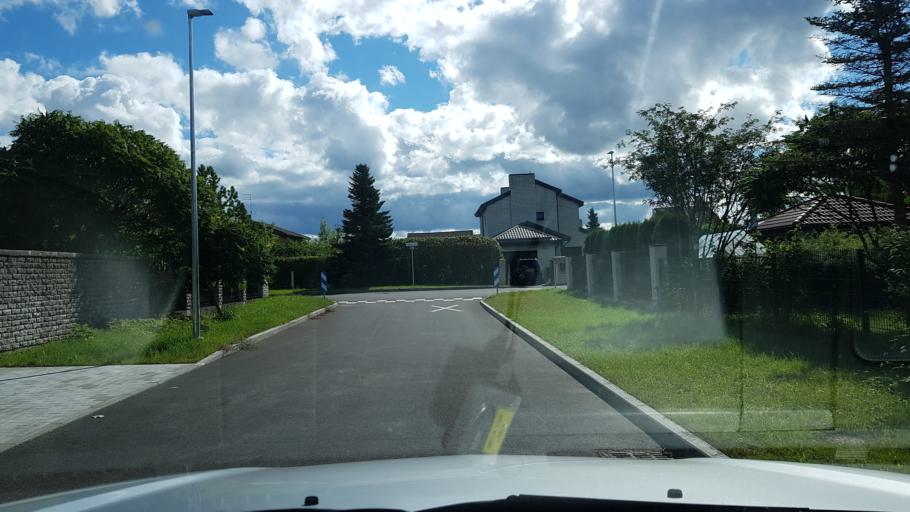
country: EE
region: Harju
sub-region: Tallinna linn
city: Tallinn
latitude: 59.3884
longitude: 24.7958
